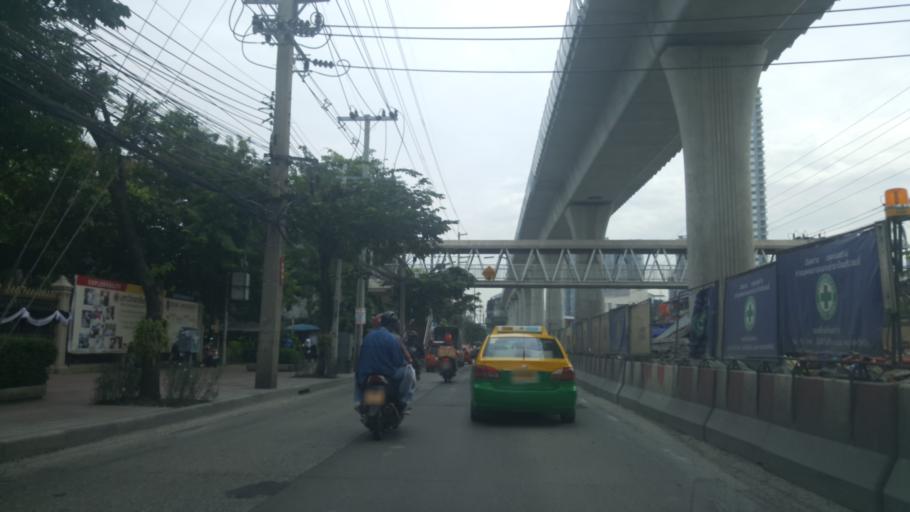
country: TH
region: Bangkok
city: Phasi Charoen
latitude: 13.7183
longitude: 100.4532
